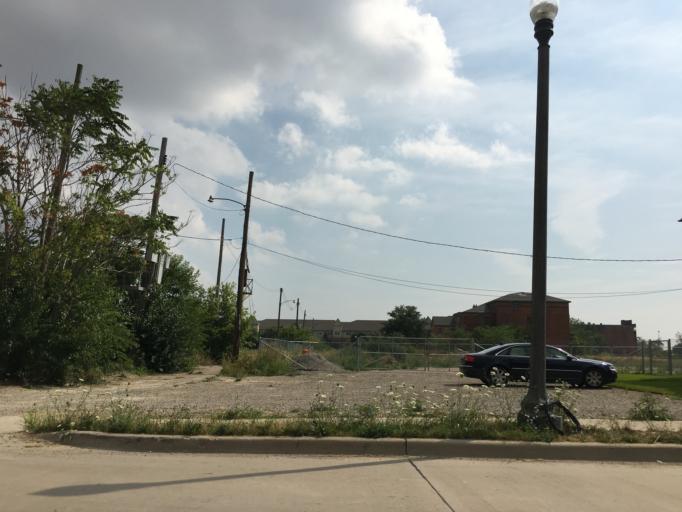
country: US
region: Michigan
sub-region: Wayne County
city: Detroit
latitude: 42.3442
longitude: -83.0530
